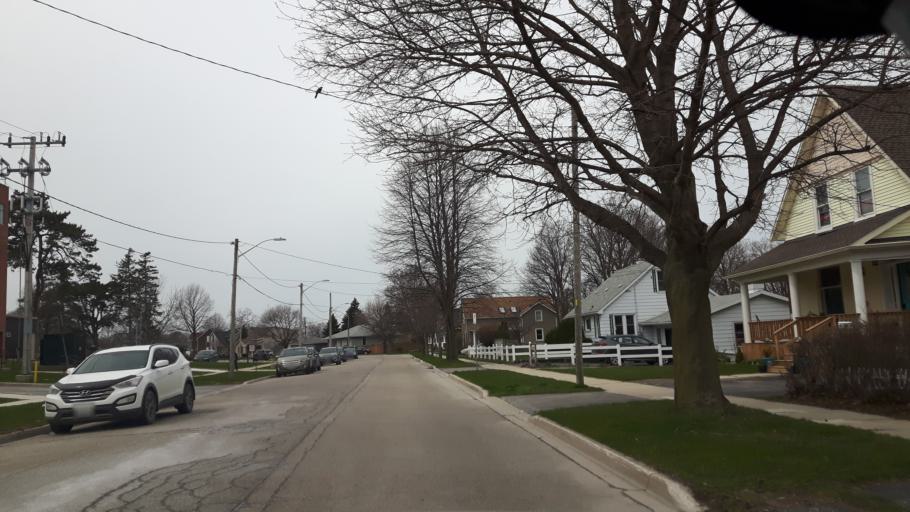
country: CA
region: Ontario
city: Goderich
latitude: 43.7503
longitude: -81.7049
